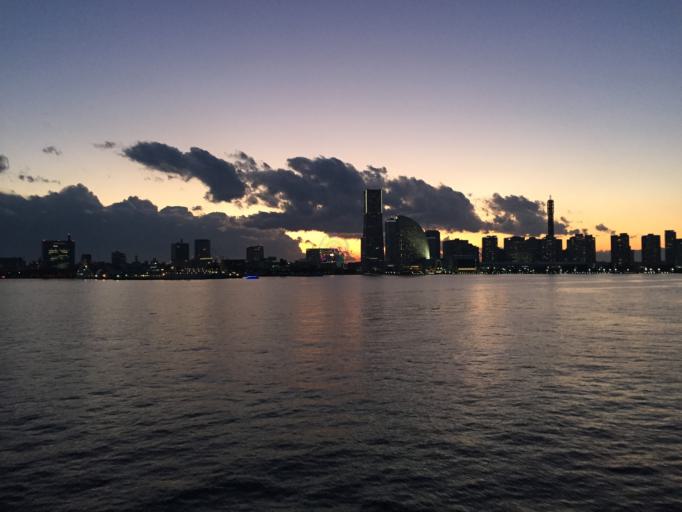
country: JP
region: Kanagawa
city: Yokohama
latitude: 35.4620
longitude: 139.6526
